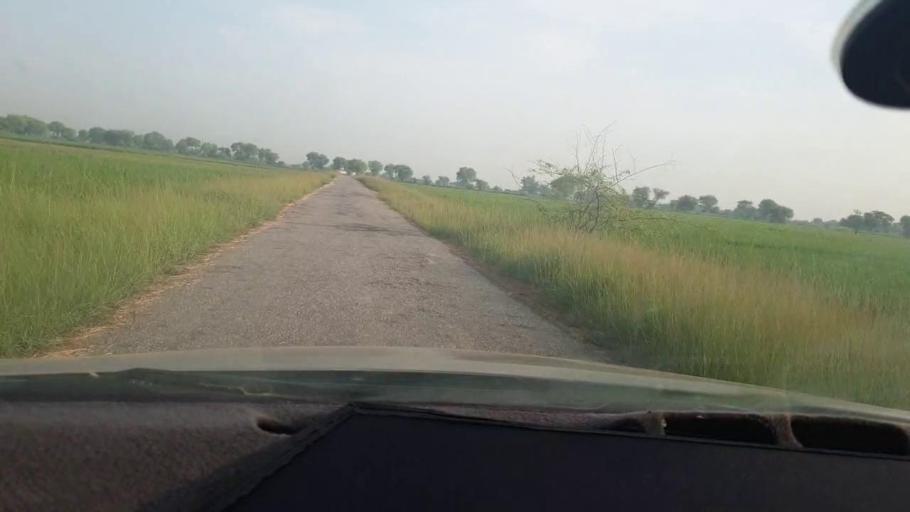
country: PK
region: Sindh
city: Jacobabad
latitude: 28.3059
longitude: 68.4146
